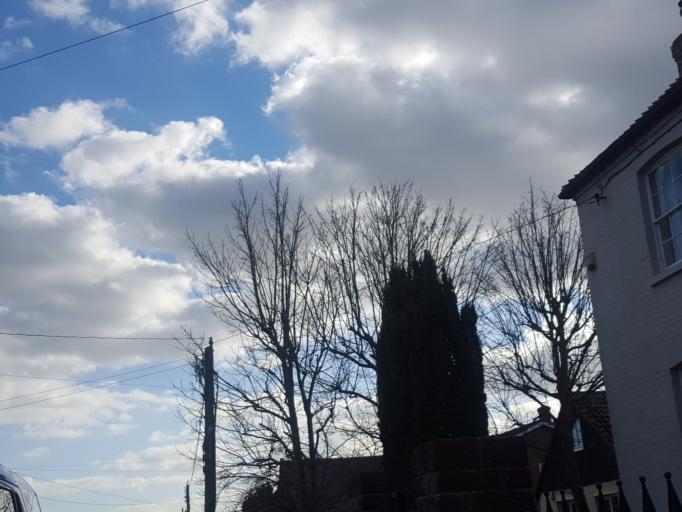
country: GB
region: England
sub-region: Essex
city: Little Clacton
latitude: 51.8585
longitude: 1.1164
